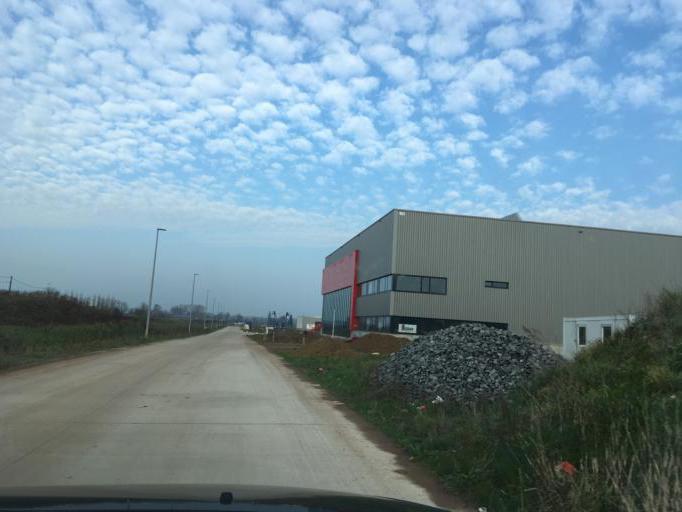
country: BE
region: Flanders
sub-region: Provincie West-Vlaanderen
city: Roeselare
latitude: 50.9464
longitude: 3.0907
